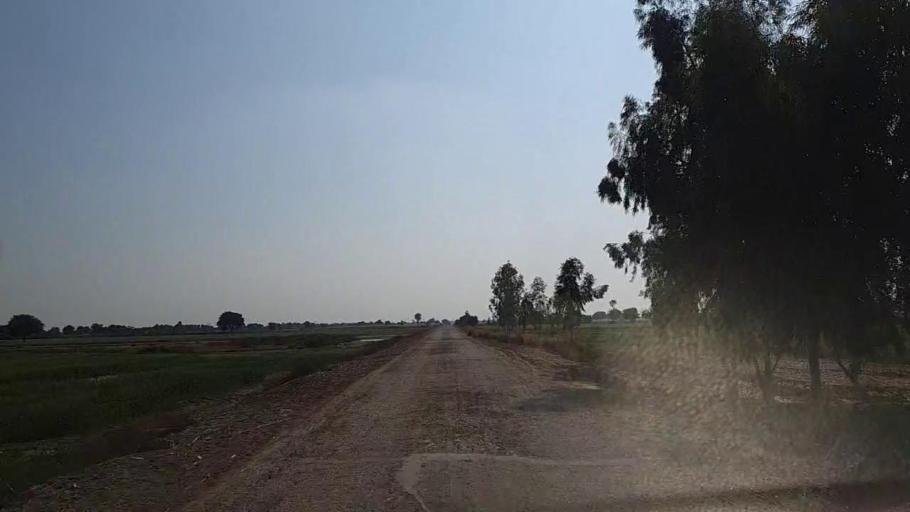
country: PK
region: Sindh
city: Jam Sahib
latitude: 26.2682
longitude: 68.5672
